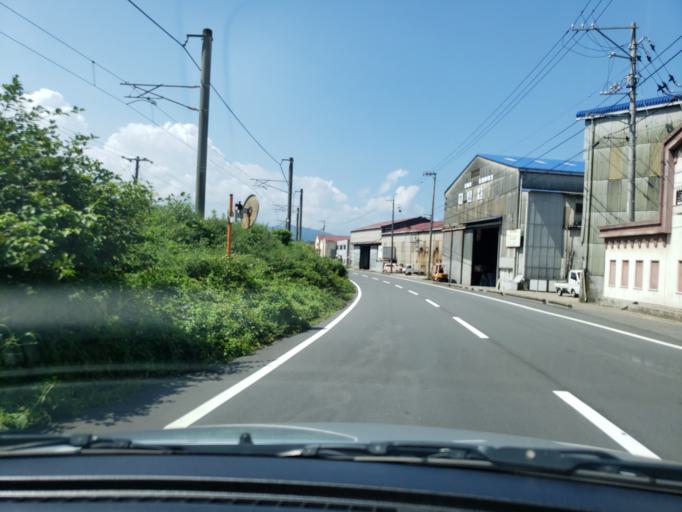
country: JP
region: Ehime
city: Hojo
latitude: 34.0922
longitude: 132.9331
